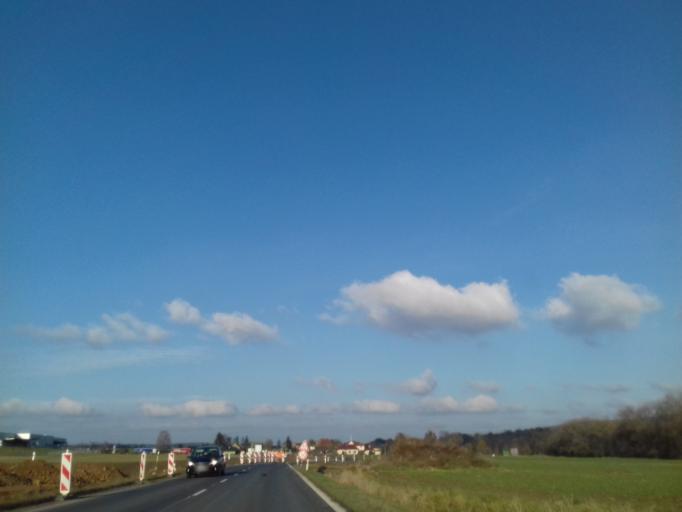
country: CZ
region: Plzensky
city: Stankov
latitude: 49.5638
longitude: 13.0758
